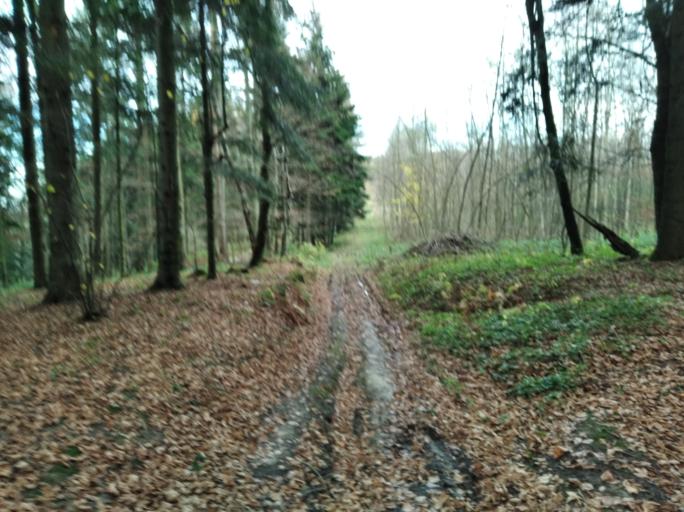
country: PL
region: Subcarpathian Voivodeship
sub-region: Powiat strzyzowski
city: Jawornik
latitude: 49.8650
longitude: 21.8558
